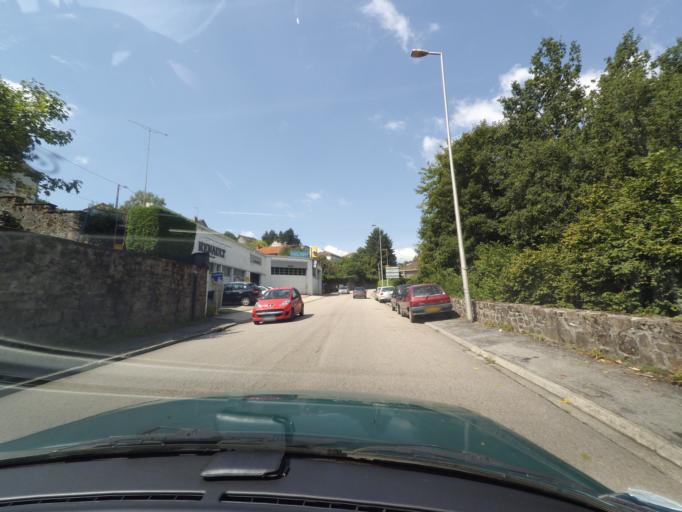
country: FR
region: Limousin
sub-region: Departement de la Haute-Vienne
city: Eymoutiers
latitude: 45.7384
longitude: 1.7382
